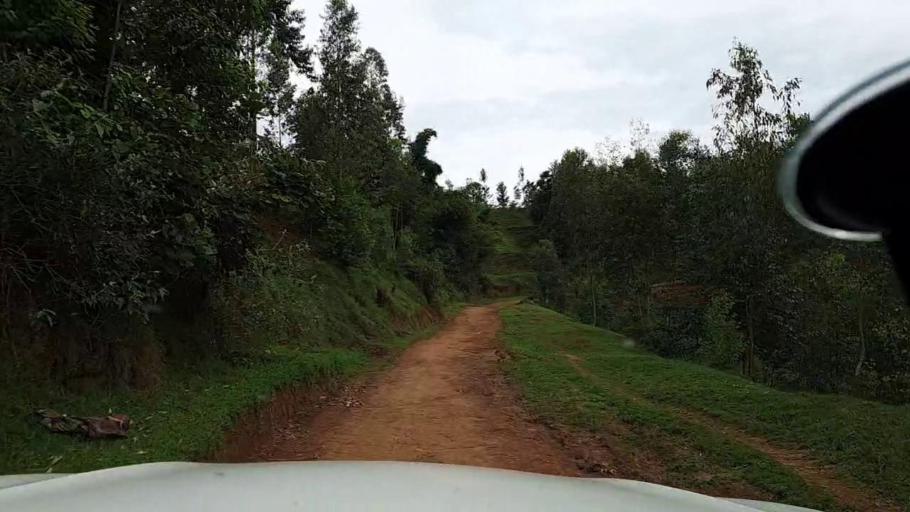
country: RW
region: Southern Province
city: Gitarama
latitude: -2.1222
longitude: 29.6492
